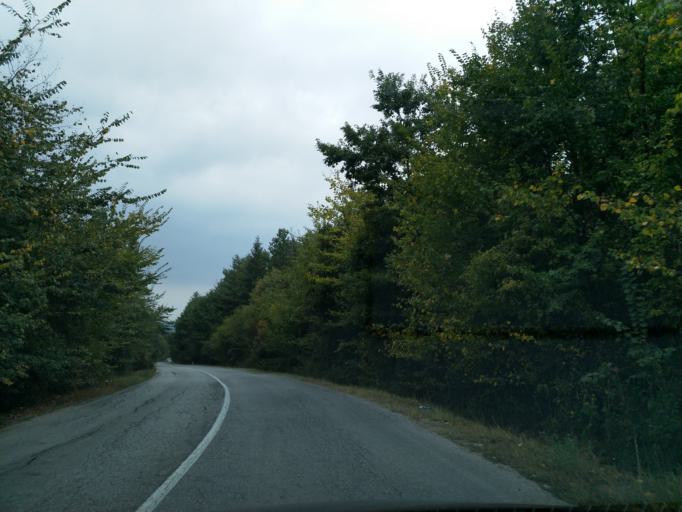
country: RS
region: Central Serbia
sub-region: Pomoravski Okrug
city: Jagodina
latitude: 44.0266
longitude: 21.1977
